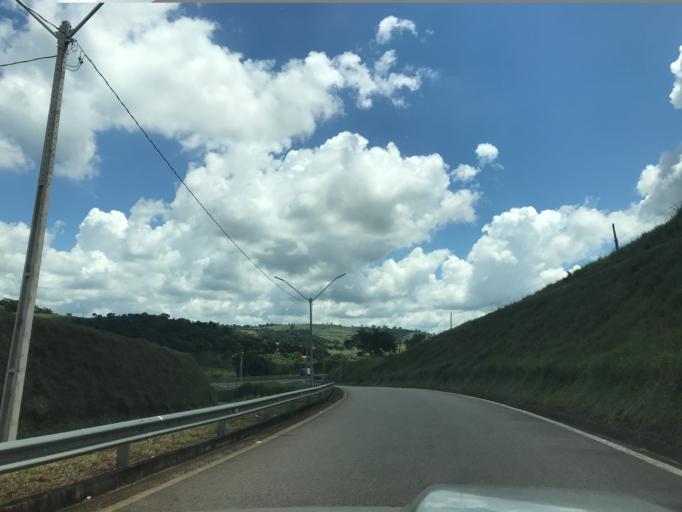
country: BR
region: Minas Gerais
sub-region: Tres Coracoes
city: Tres Coracoes
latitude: -21.6559
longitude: -45.3002
